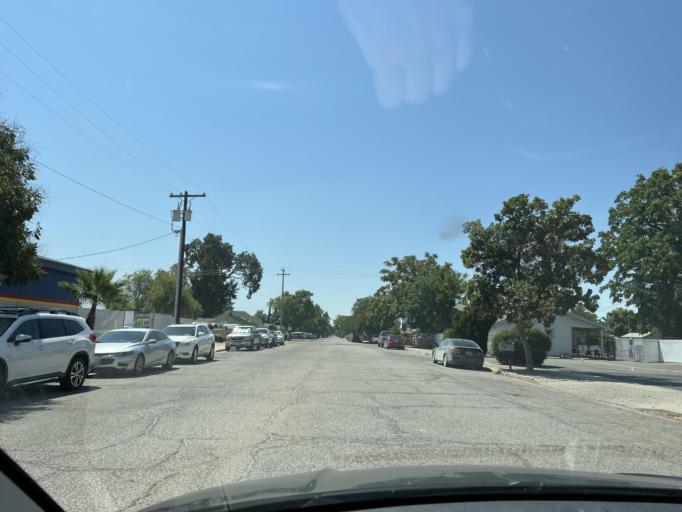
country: US
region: California
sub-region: San Luis Obispo County
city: Paso Robles
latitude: 35.6390
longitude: -120.6912
